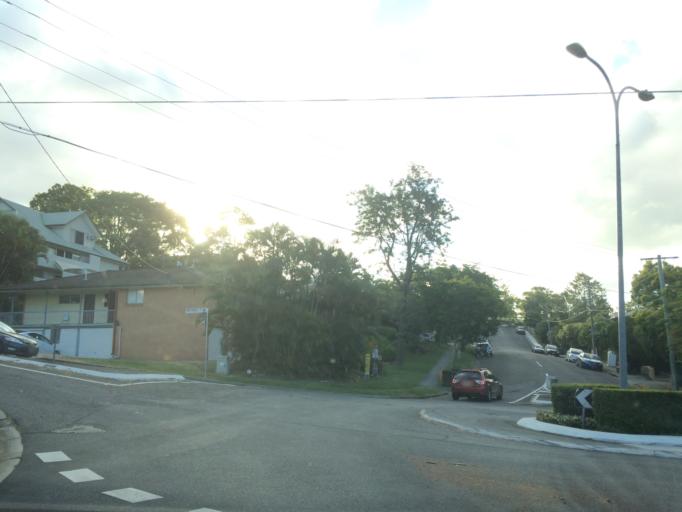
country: AU
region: Queensland
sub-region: Brisbane
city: Taringa
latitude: -27.4921
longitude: 152.9870
